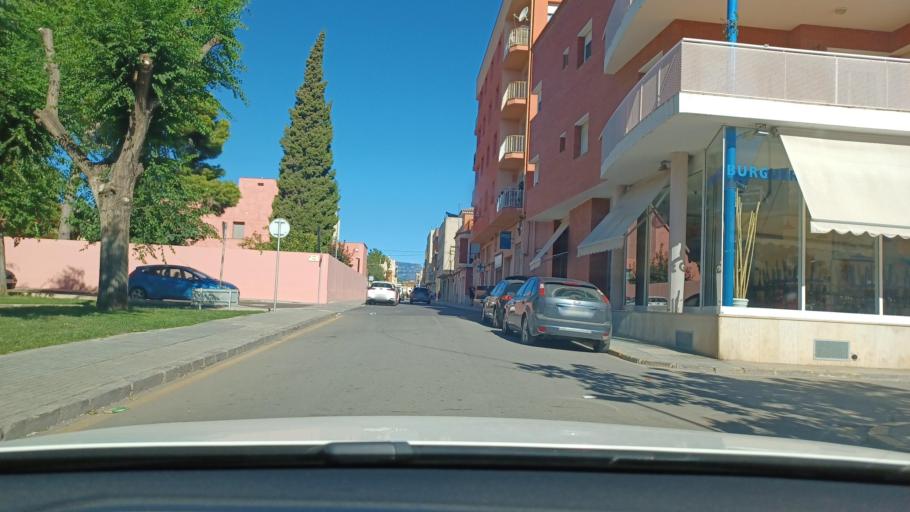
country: ES
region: Catalonia
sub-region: Provincia de Tarragona
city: Amposta
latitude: 40.7132
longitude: 0.5774
